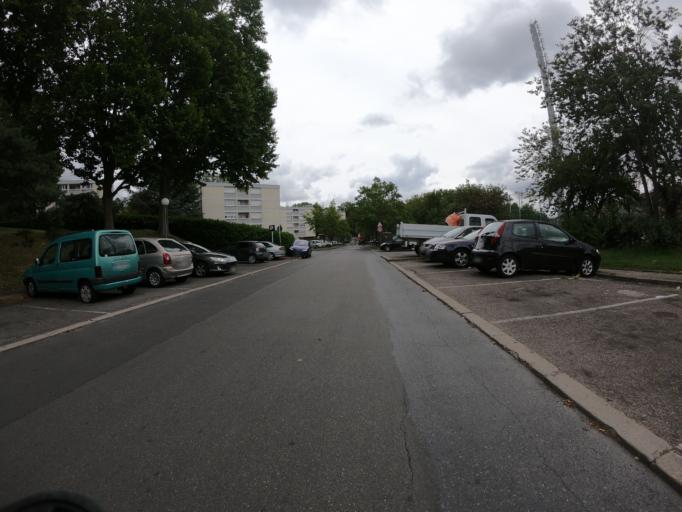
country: FR
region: Ile-de-France
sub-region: Departement du Val-de-Marne
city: Fresnes
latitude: 48.7646
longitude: 2.3239
